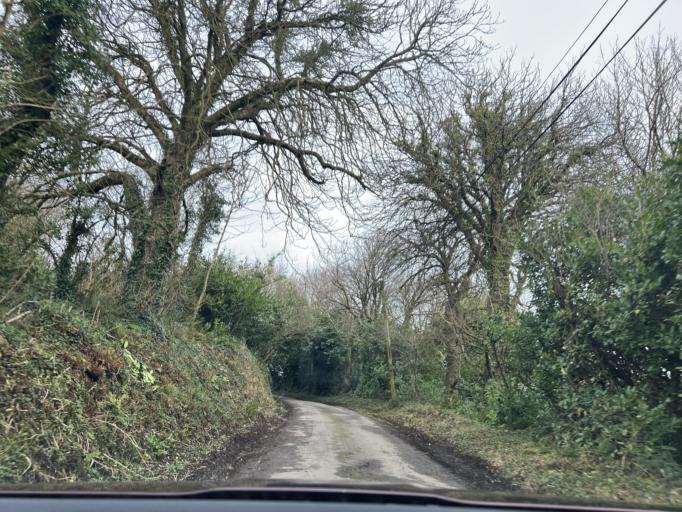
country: IE
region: Leinster
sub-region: Loch Garman
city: Loch Garman
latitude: 52.3736
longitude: -6.5402
